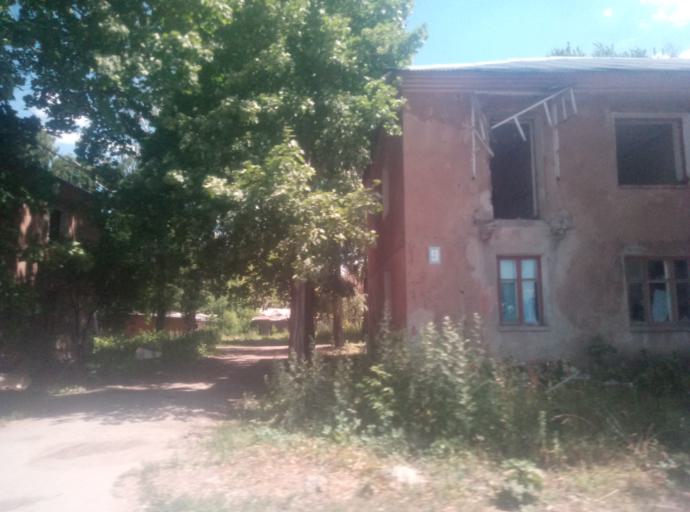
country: RU
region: Tula
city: Kireyevsk
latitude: 53.9255
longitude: 37.9226
